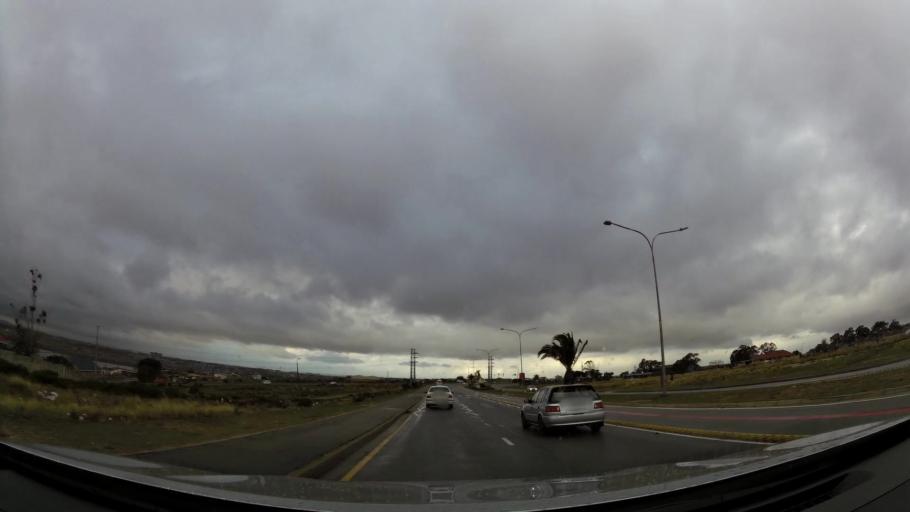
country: ZA
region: Eastern Cape
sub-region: Nelson Mandela Bay Metropolitan Municipality
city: Port Elizabeth
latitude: -33.8959
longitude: 25.5367
